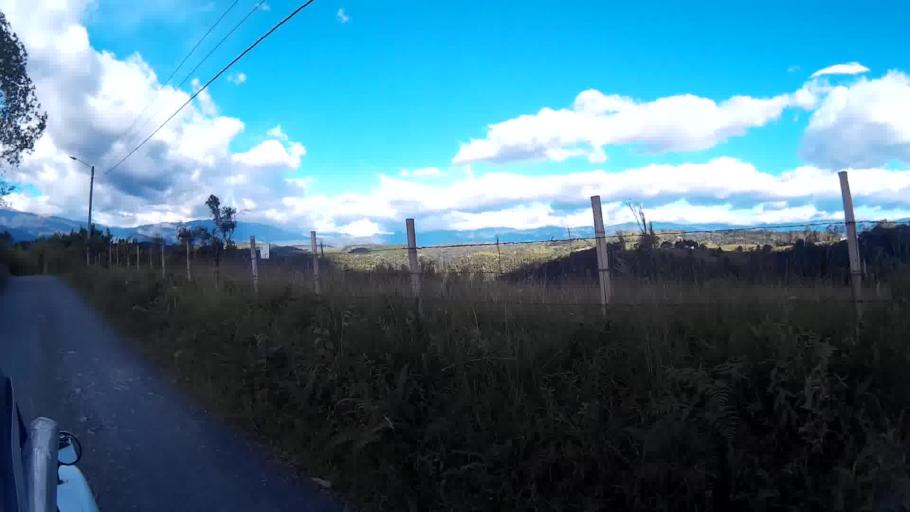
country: CO
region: Quindio
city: Filandia
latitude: 4.7110
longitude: -75.6499
